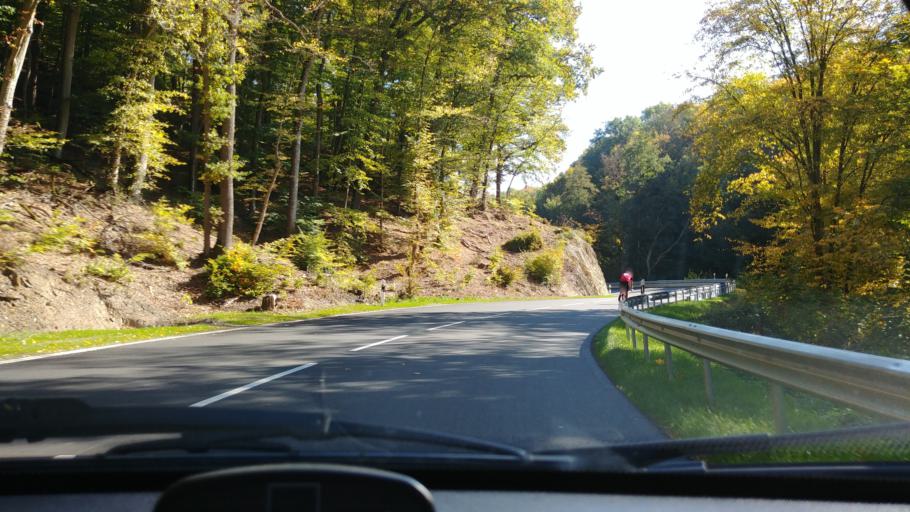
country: DE
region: Rheinland-Pfalz
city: Mudershausen
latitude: 50.2866
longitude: 8.0477
